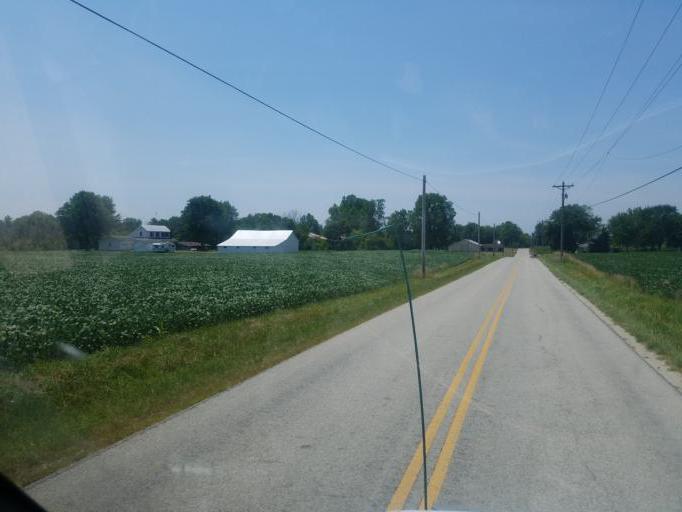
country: US
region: Ohio
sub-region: Shelby County
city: Fort Loramie
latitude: 40.3290
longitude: -84.3665
